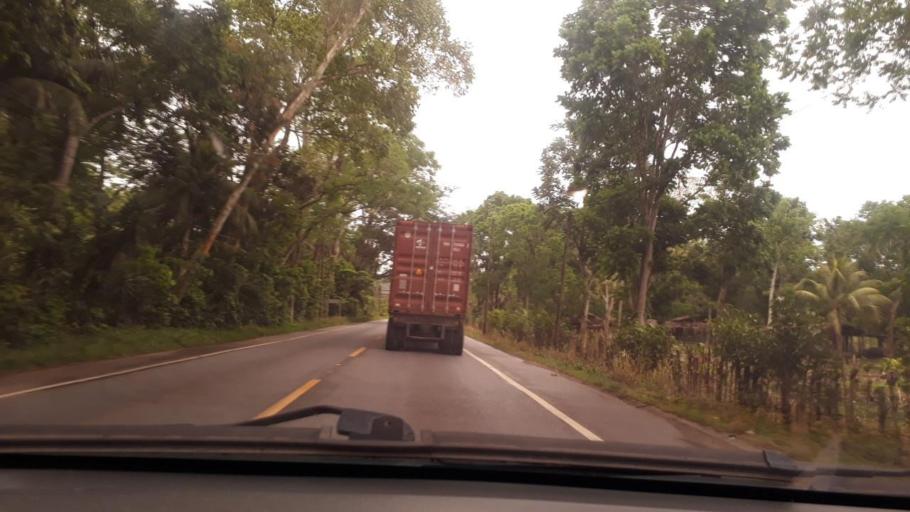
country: GT
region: Izabal
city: Morales
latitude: 15.5473
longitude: -88.6954
